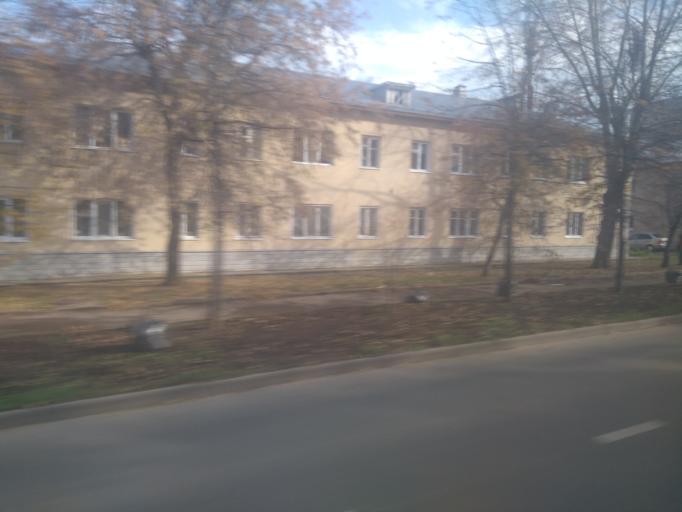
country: RU
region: Tatarstan
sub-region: Gorod Kazan'
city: Kazan
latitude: 55.8000
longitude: 49.1898
